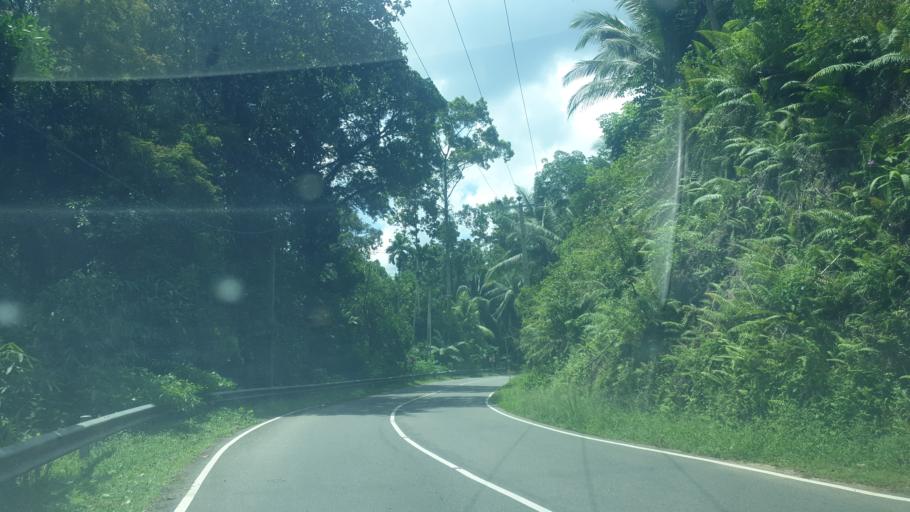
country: LK
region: Western
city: Horawala Junction
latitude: 6.5434
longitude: 80.2801
